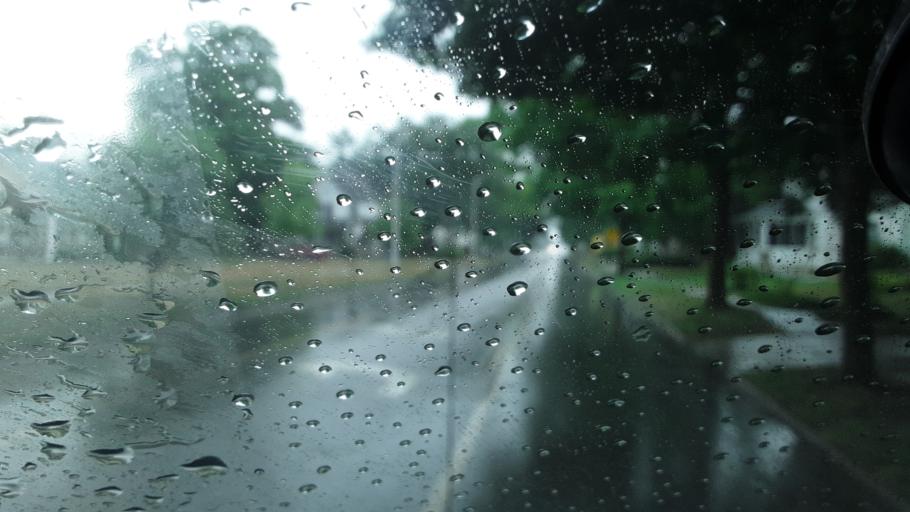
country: US
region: Ohio
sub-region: Williams County
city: Montpelier
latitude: 41.5865
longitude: -84.6044
